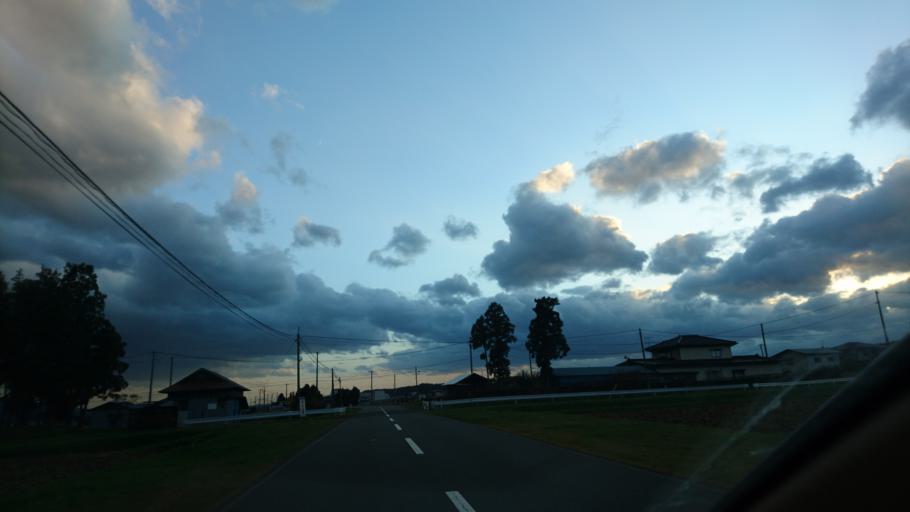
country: JP
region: Iwate
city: Mizusawa
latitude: 39.1046
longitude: 141.1482
